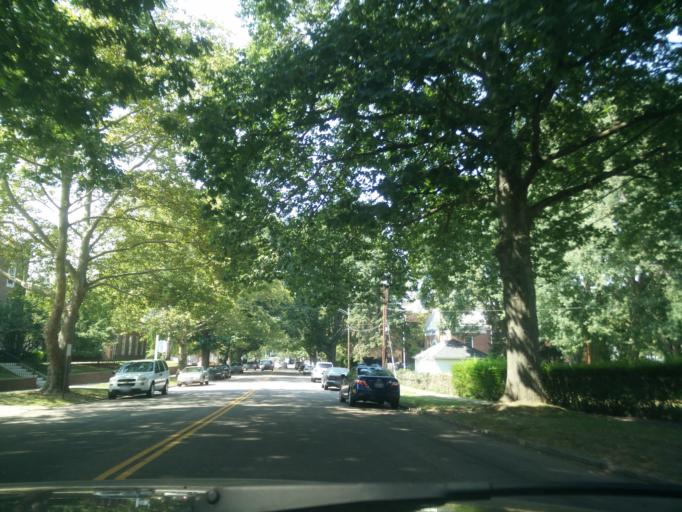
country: US
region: Connecticut
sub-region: Fairfield County
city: Fairfield
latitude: 41.1435
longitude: -73.2500
